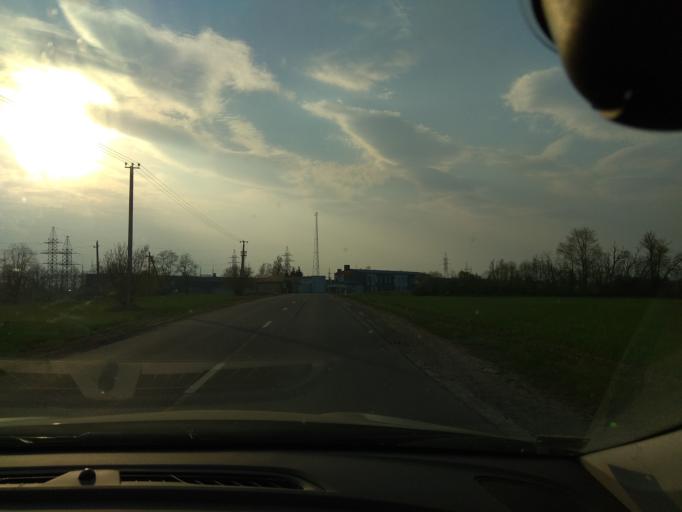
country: LT
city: Baltoji Voke
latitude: 54.6108
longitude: 25.1233
